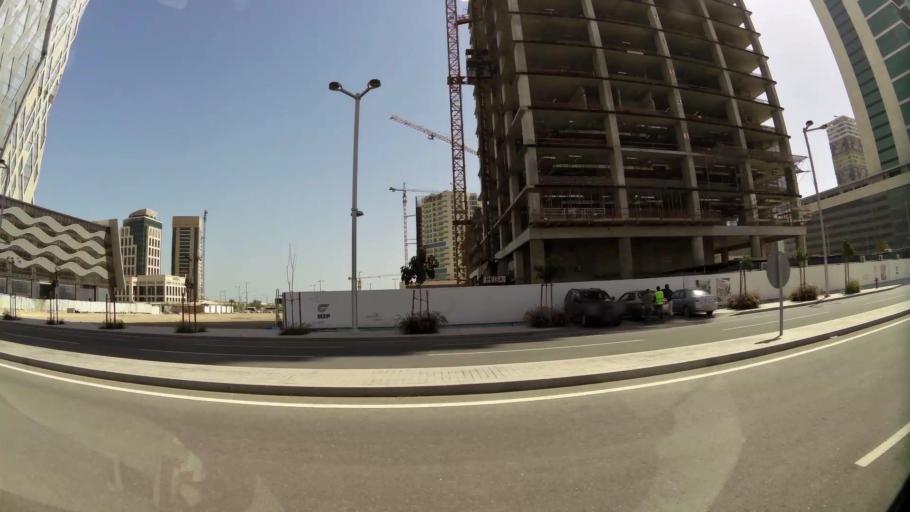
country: QA
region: Baladiyat ad Dawhah
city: Doha
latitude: 25.3900
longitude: 51.5198
